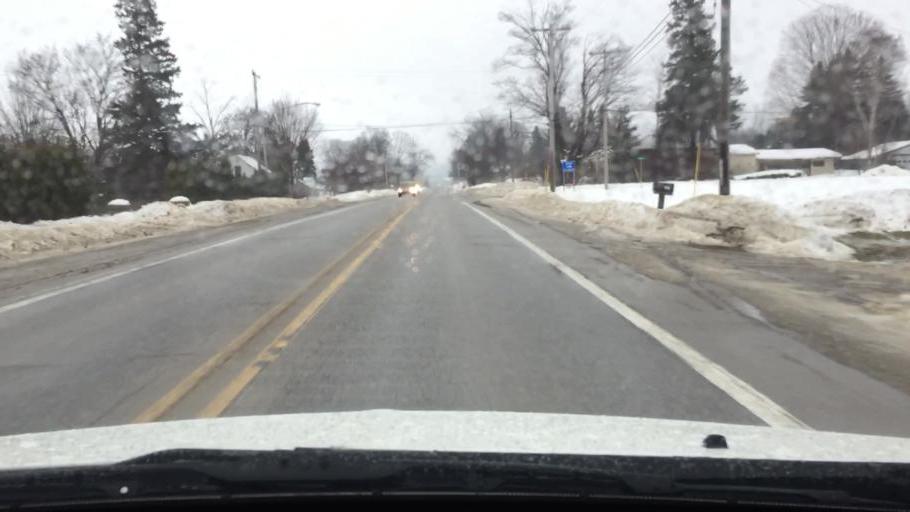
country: US
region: Michigan
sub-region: Charlevoix County
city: East Jordan
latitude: 45.1476
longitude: -85.1399
